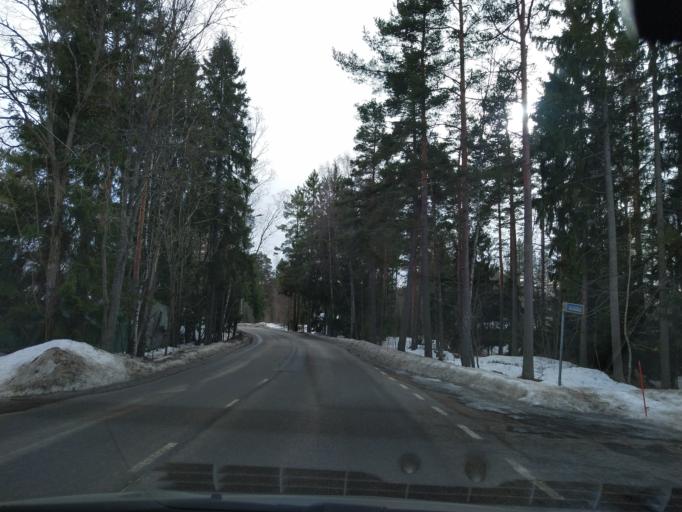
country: FI
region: Uusimaa
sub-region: Helsinki
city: Sibbo
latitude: 60.2698
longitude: 25.2854
